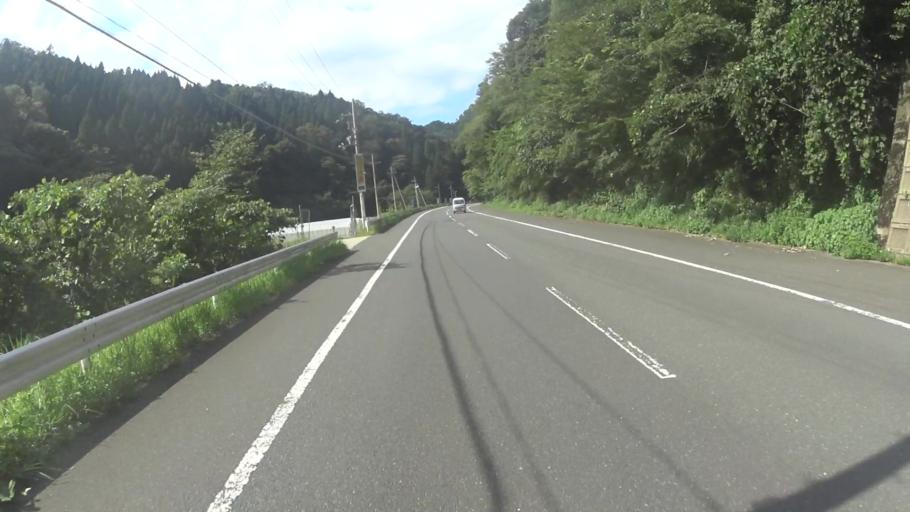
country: JP
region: Kyoto
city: Miyazu
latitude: 35.7336
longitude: 135.2569
